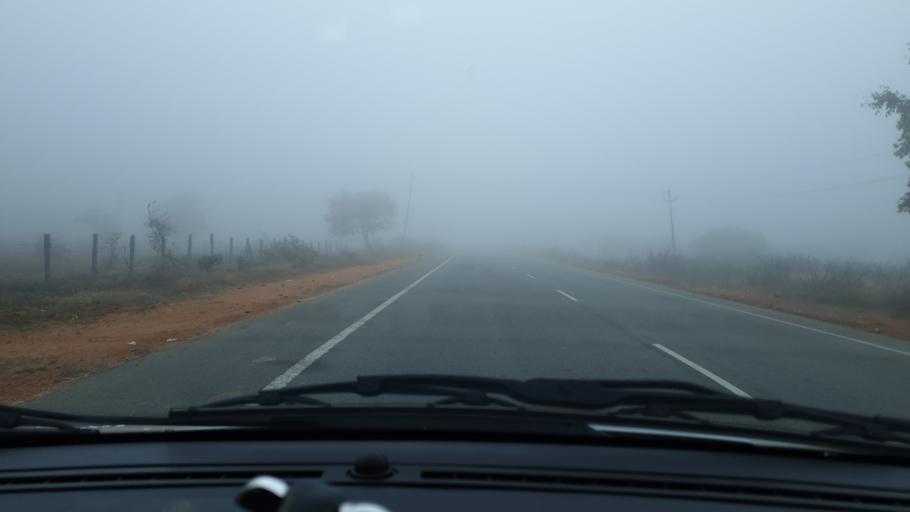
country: IN
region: Telangana
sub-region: Mahbubnagar
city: Nagar Karnul
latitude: 16.6877
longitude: 78.5224
